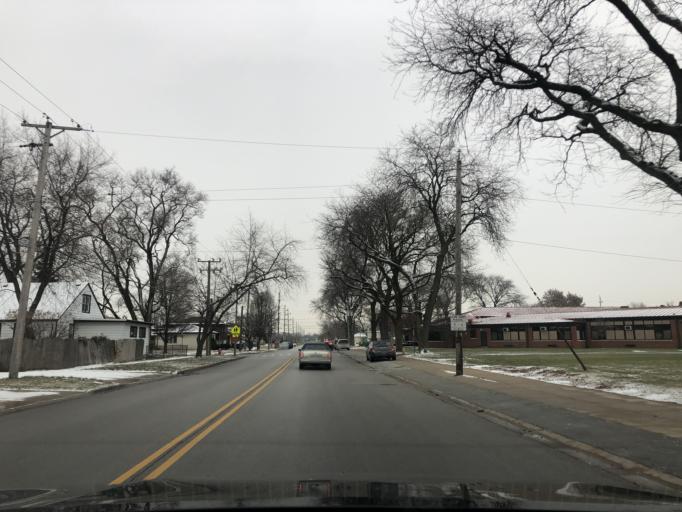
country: US
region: Illinois
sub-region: Cook County
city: Evergreen Park
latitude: 41.7298
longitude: -87.6922
